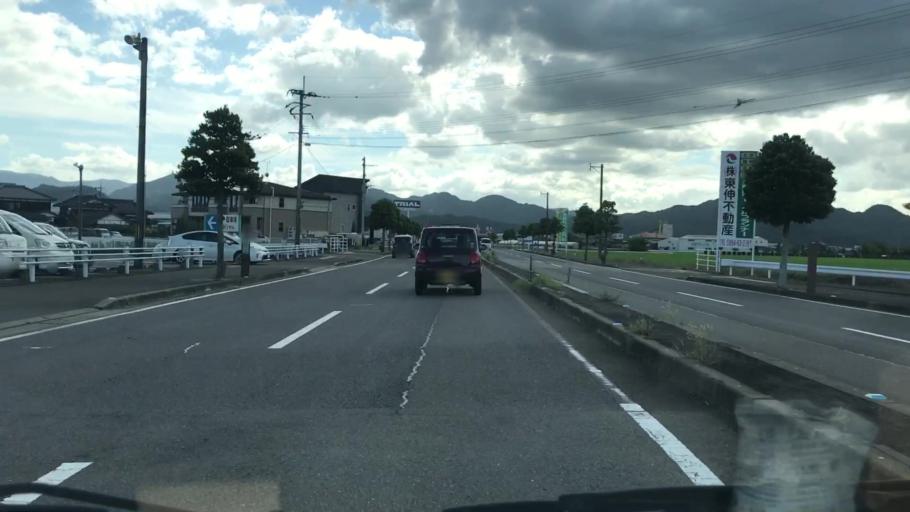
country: JP
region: Saga Prefecture
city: Kashima
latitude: 33.1250
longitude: 130.0997
